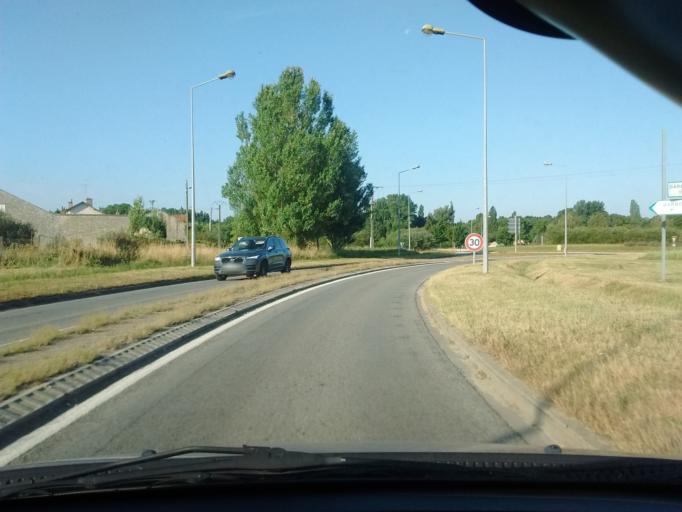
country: FR
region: Ile-de-France
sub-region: Departement de l'Essonne
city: Milly-la-Foret
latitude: 48.4184
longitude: 2.4660
